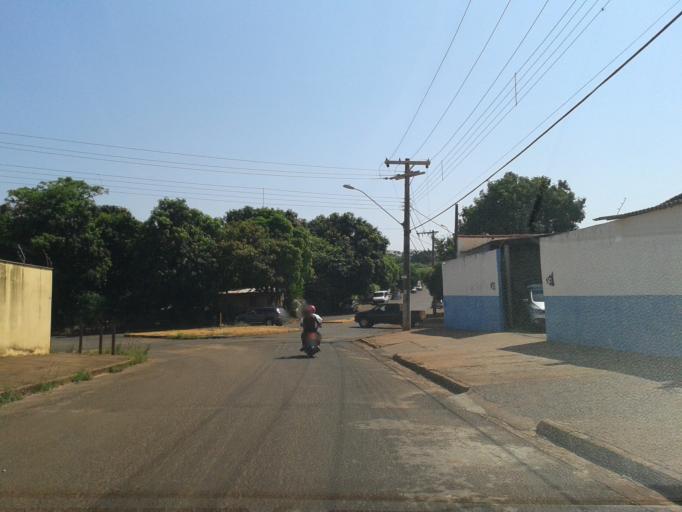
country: BR
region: Minas Gerais
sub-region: Ituiutaba
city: Ituiutaba
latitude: -18.9582
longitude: -49.4516
